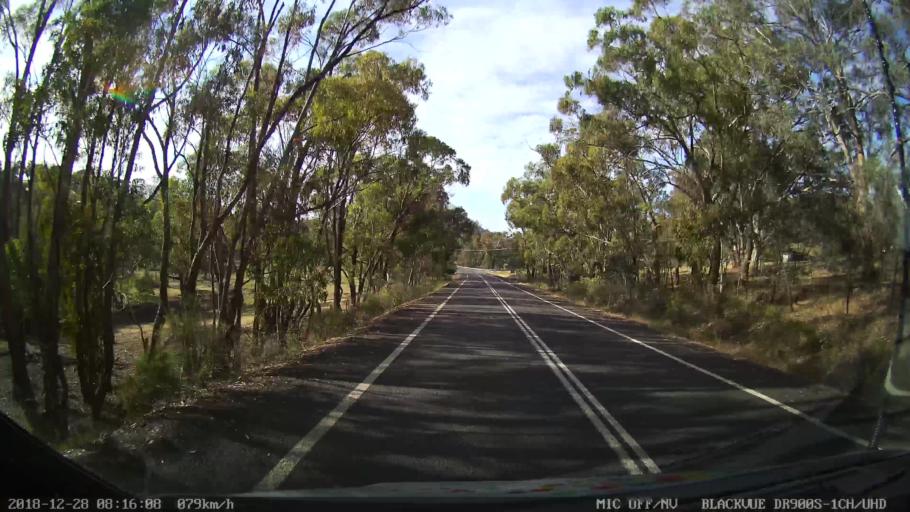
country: AU
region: New South Wales
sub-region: Blayney
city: Blayney
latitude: -33.8298
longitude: 149.3290
